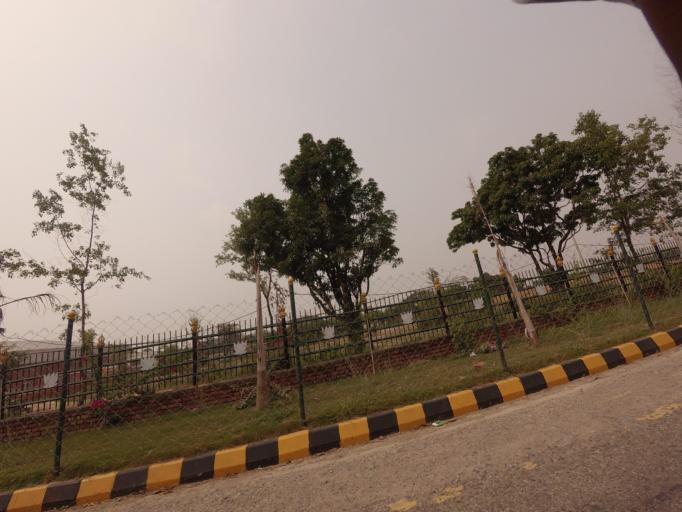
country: IN
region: Uttar Pradesh
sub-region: Maharajganj
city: Nautanwa
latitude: 27.4914
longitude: 83.2789
